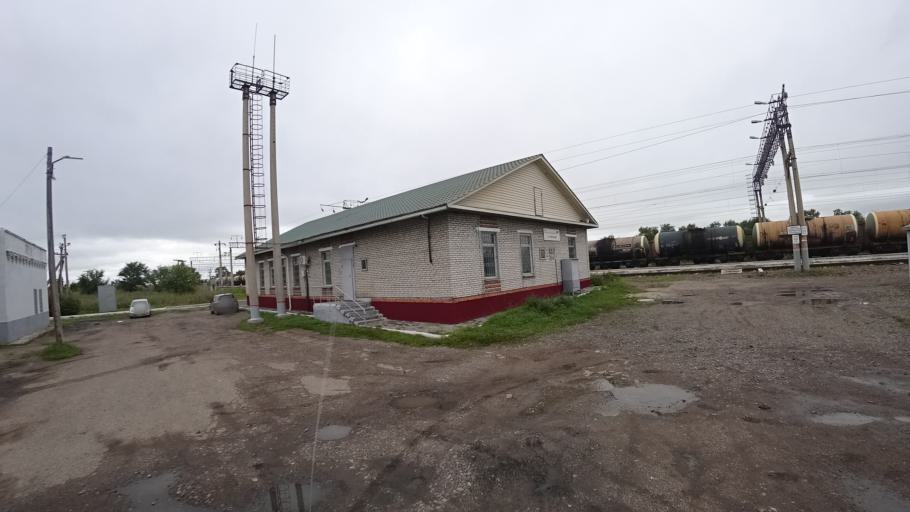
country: RU
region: Primorskiy
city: Chernigovka
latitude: 44.3396
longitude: 132.5336
